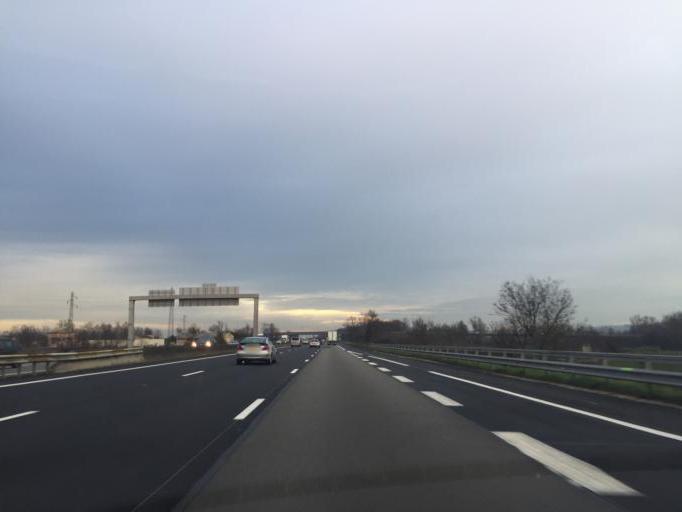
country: FR
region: Rhone-Alpes
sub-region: Departement du Rhone
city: Belleville
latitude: 46.1027
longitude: 4.7529
